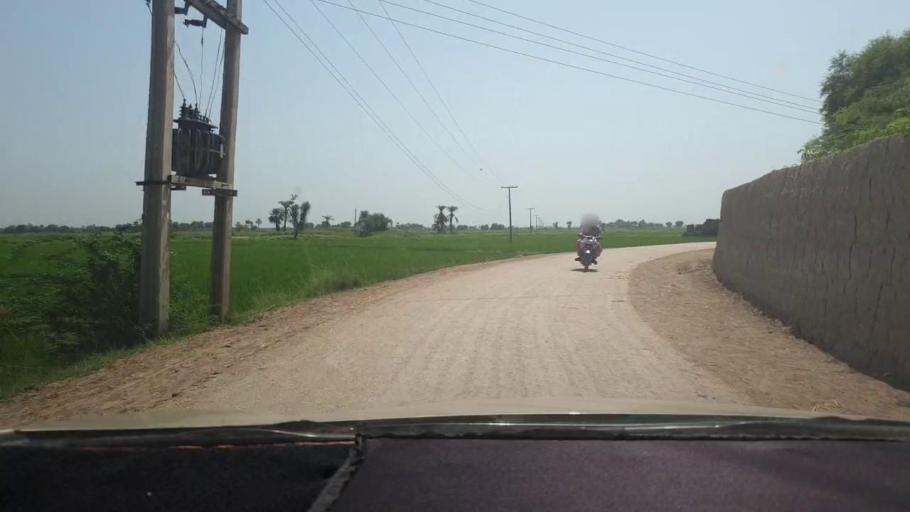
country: PK
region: Sindh
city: Miro Khan
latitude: 27.6692
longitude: 68.0994
